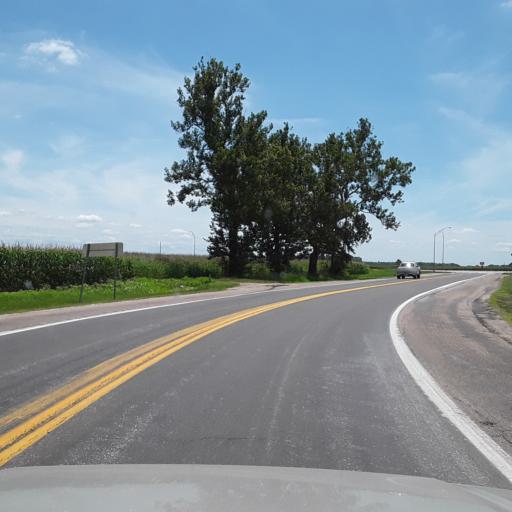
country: US
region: Nebraska
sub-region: Merrick County
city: Central City
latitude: 41.1933
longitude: -97.8724
